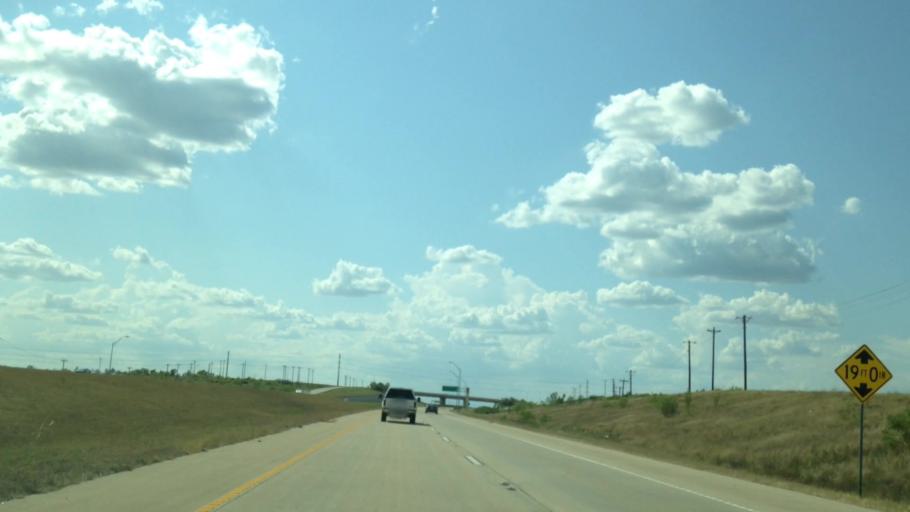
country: US
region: Texas
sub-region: Travis County
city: Onion Creek
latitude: 30.0987
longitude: -97.7740
